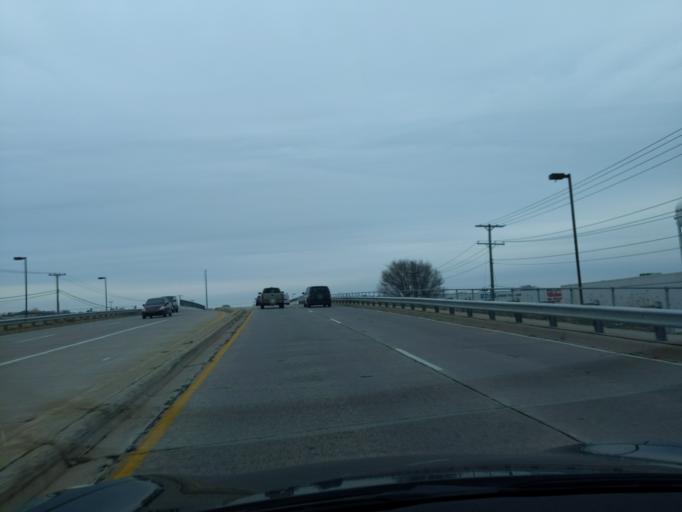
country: US
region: Indiana
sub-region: Saint Joseph County
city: Georgetown
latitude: 41.7150
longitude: -86.1876
